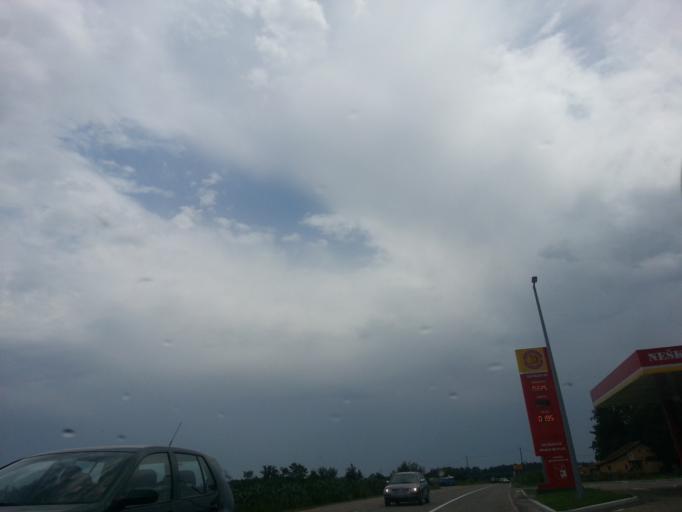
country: BA
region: Republika Srpska
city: Velika Obarska
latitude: 44.7737
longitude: 19.1174
